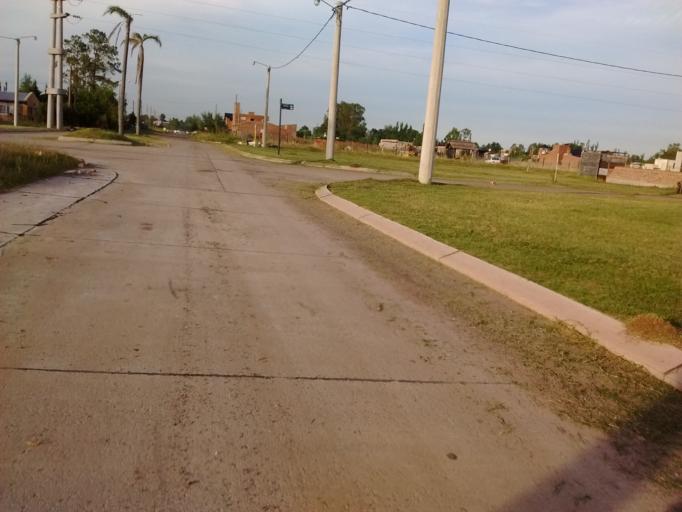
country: AR
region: Santa Fe
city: Roldan
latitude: -32.9245
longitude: -60.8735
